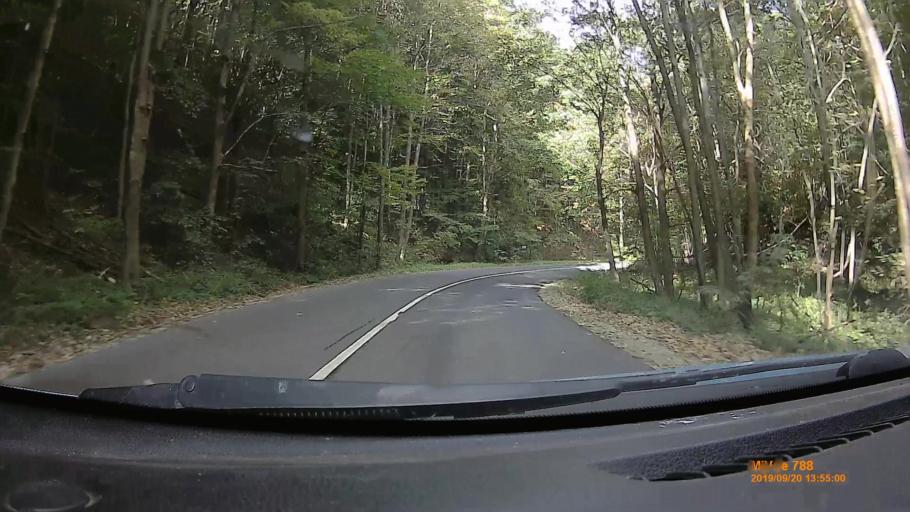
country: HU
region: Borsod-Abauj-Zemplen
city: Saly
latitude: 48.0786
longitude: 20.6150
